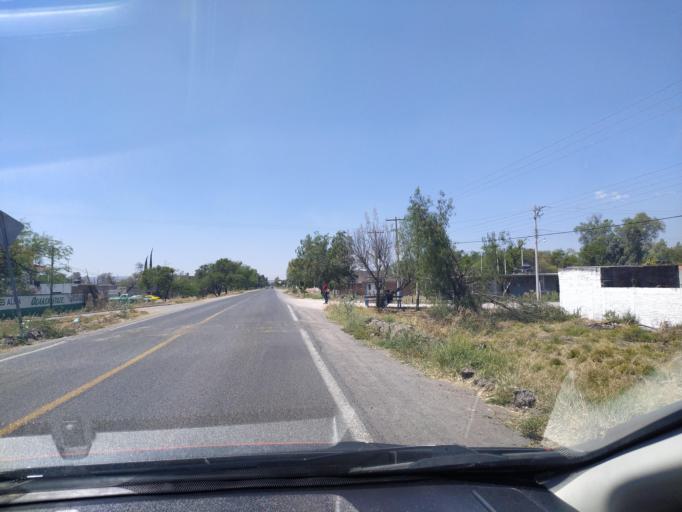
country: MX
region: Guanajuato
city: Ciudad Manuel Doblado
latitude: 20.7406
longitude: -101.8826
